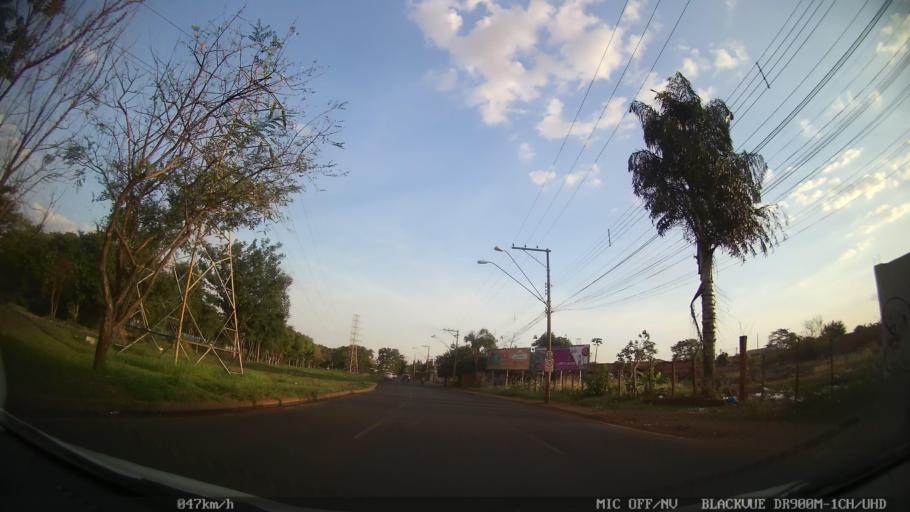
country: BR
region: Sao Paulo
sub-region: Ribeirao Preto
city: Ribeirao Preto
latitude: -21.1489
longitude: -47.8084
